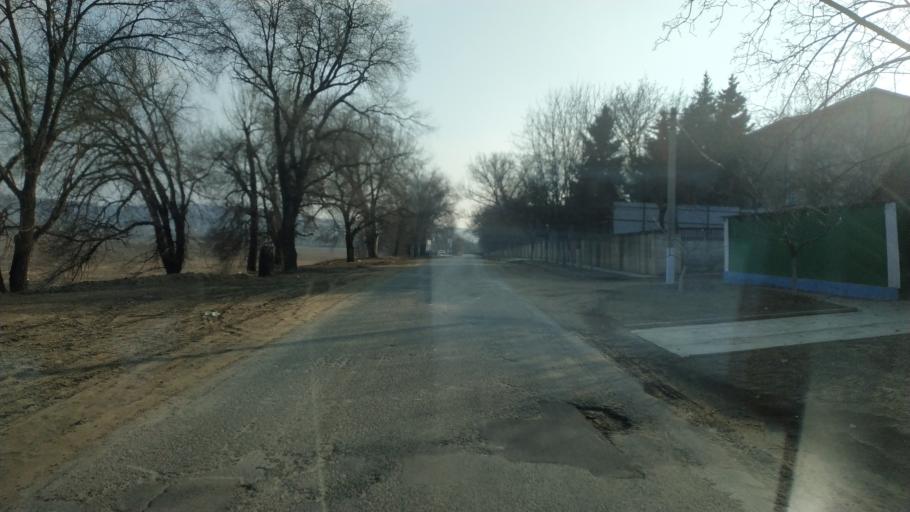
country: MD
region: Hincesti
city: Dancu
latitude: 46.7708
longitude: 28.3464
